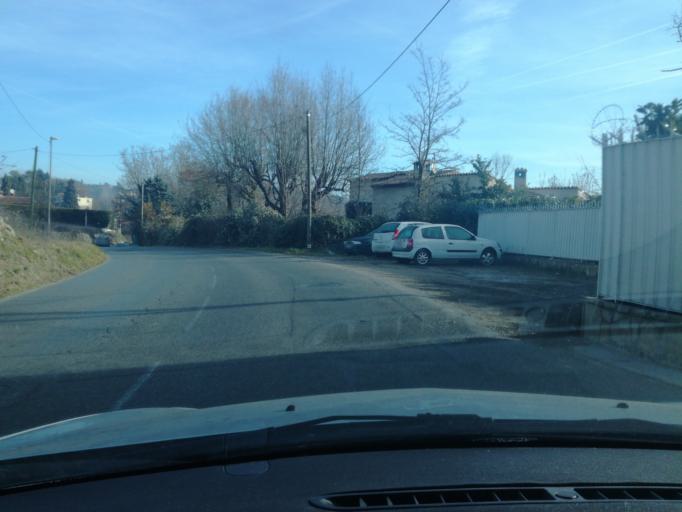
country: FR
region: Provence-Alpes-Cote d'Azur
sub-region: Departement des Alpes-Maritimes
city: Valbonne
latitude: 43.6409
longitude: 6.9973
